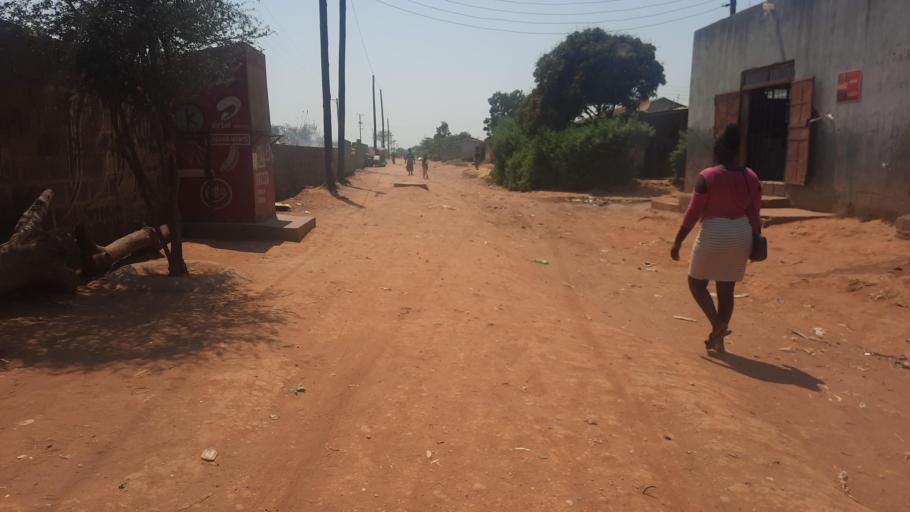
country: ZM
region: Lusaka
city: Lusaka
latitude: -15.3928
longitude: 28.3805
